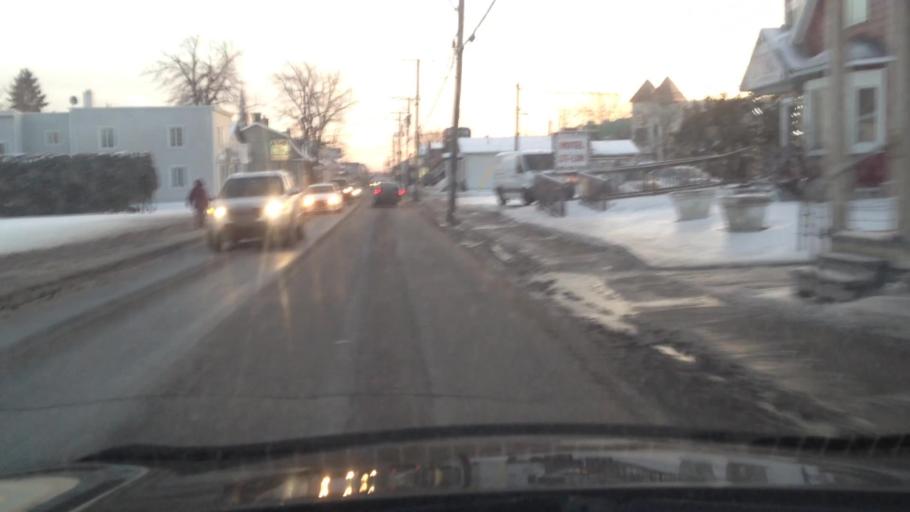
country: CA
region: Quebec
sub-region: Lanaudiere
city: Saint-Lin-Laurentides
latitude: 45.8575
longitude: -73.7571
